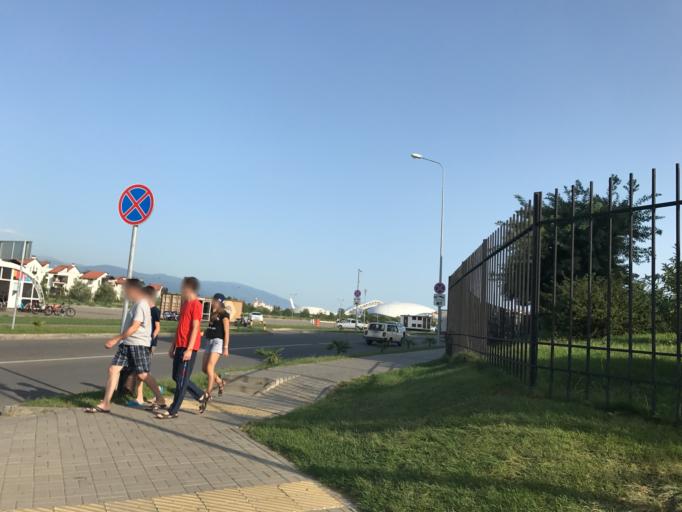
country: RU
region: Krasnodarskiy
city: Adler
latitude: 43.4114
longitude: 39.9374
